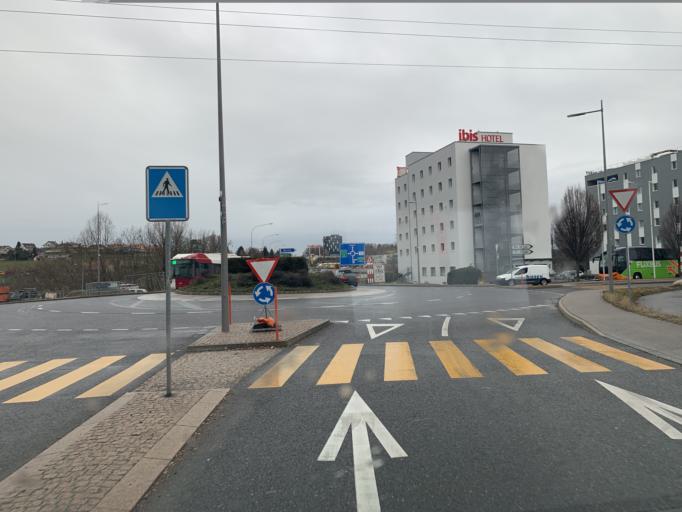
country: CH
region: Fribourg
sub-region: Sarine District
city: Fribourg
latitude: 46.8231
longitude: 7.1504
